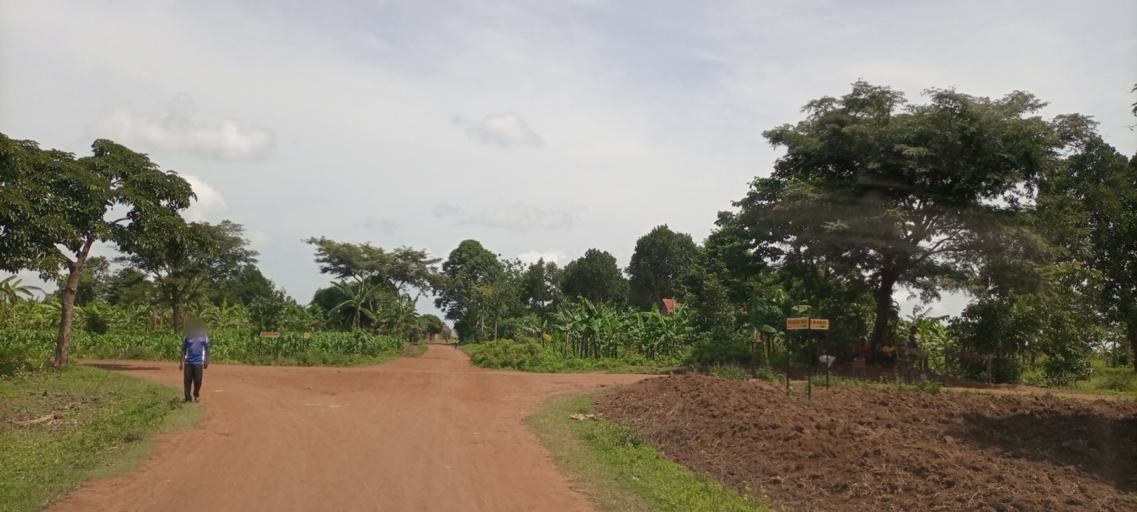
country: UG
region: Eastern Region
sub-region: Budaka District
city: Budaka
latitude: 1.1738
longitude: 33.9291
